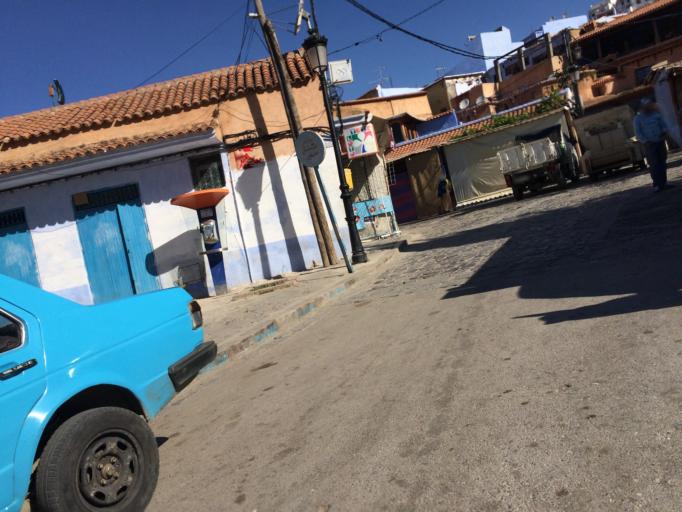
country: MA
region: Tanger-Tetouan
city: Chefchaouene
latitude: 35.1689
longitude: -5.2609
